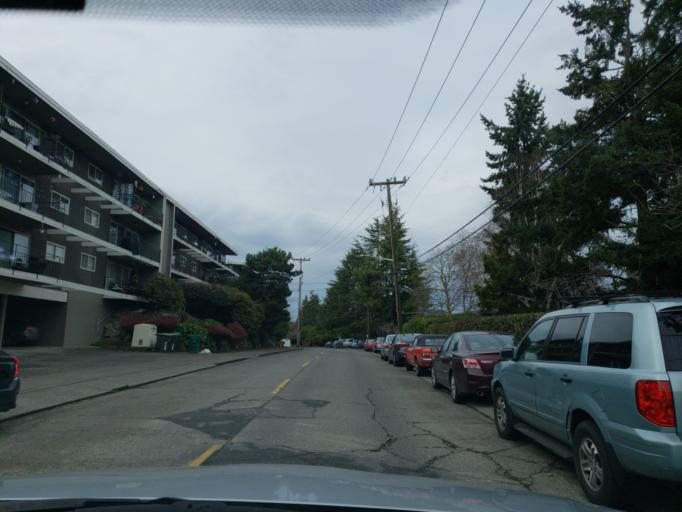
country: US
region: Washington
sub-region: King County
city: Seattle
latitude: 47.6638
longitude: -122.3973
